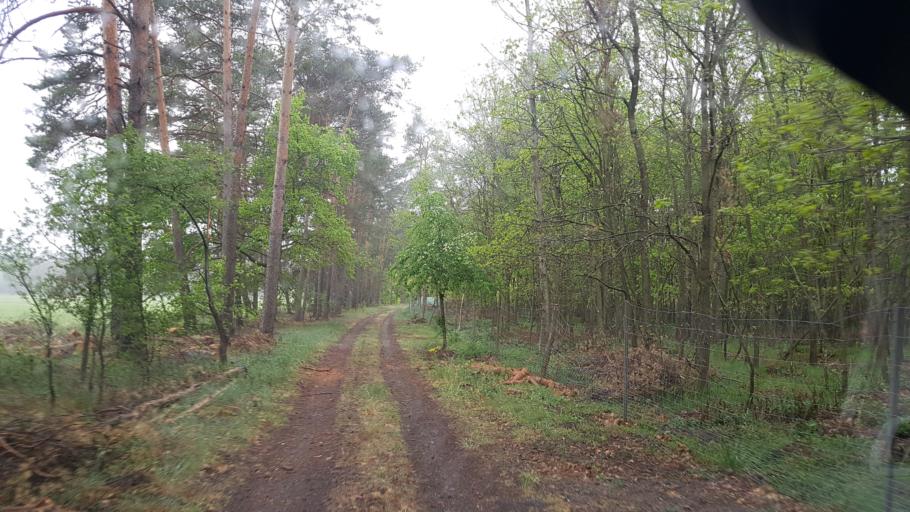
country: DE
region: Brandenburg
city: Sonnewalde
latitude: 51.7238
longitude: 13.6792
